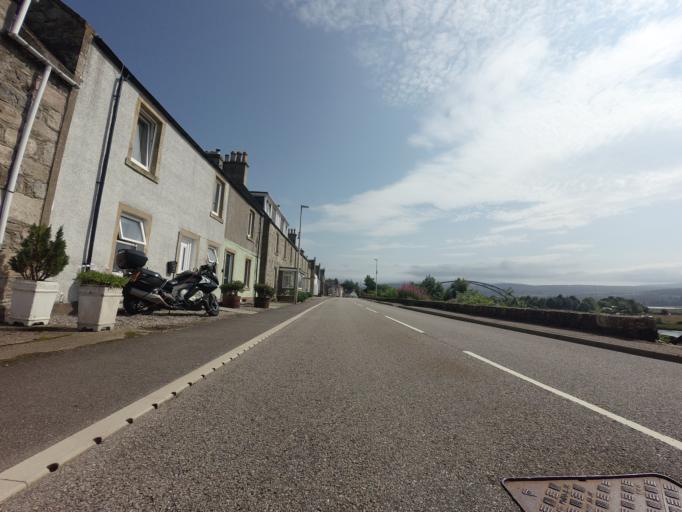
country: GB
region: Scotland
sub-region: Highland
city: Alness
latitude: 57.8938
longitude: -4.3473
